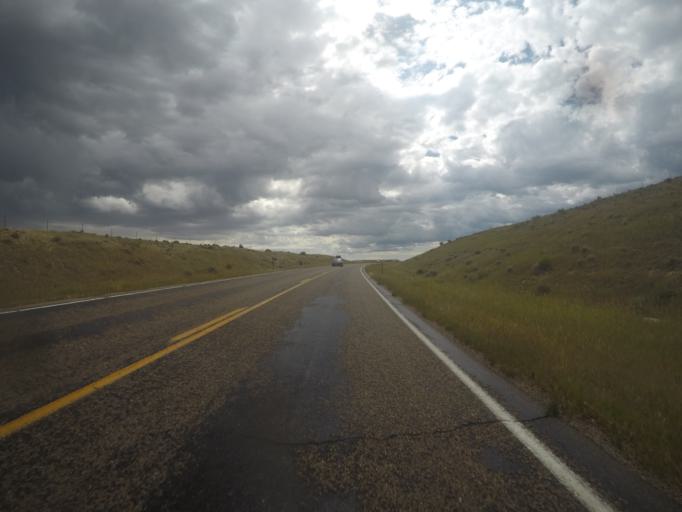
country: US
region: Utah
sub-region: Daggett County
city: Manila
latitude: 41.0272
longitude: -109.8723
